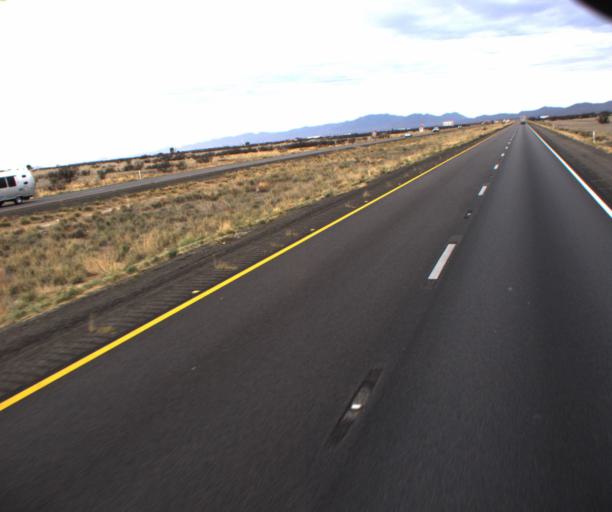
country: US
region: Arizona
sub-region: Cochise County
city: Willcox
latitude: 32.2393
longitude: -109.8652
